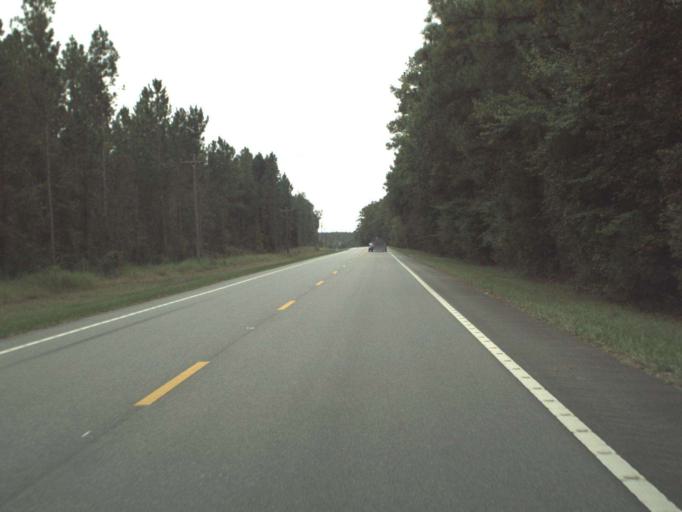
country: US
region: Florida
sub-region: Jackson County
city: Sneads
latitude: 30.6125
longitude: -85.0298
